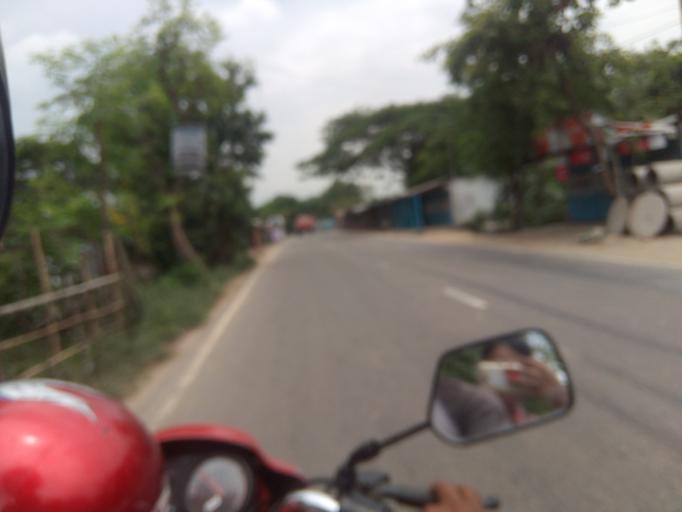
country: BD
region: Dhaka
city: Paltan
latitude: 23.7404
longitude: 90.4794
